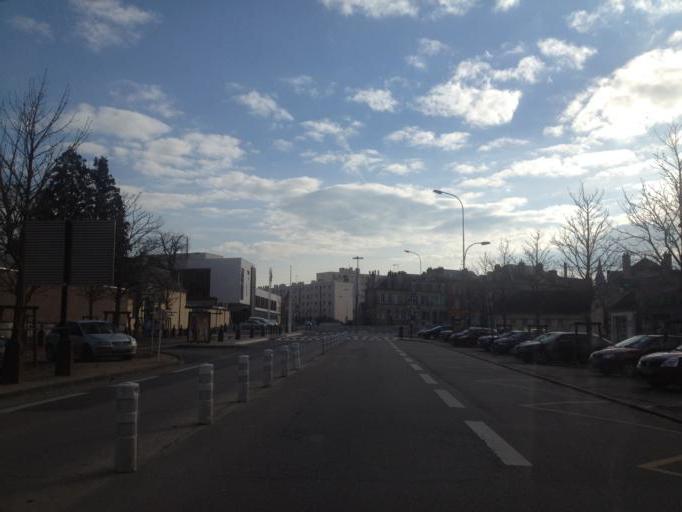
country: FR
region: Auvergne
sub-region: Departement de l'Allier
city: Moulins
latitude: 46.5689
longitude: 3.3263
